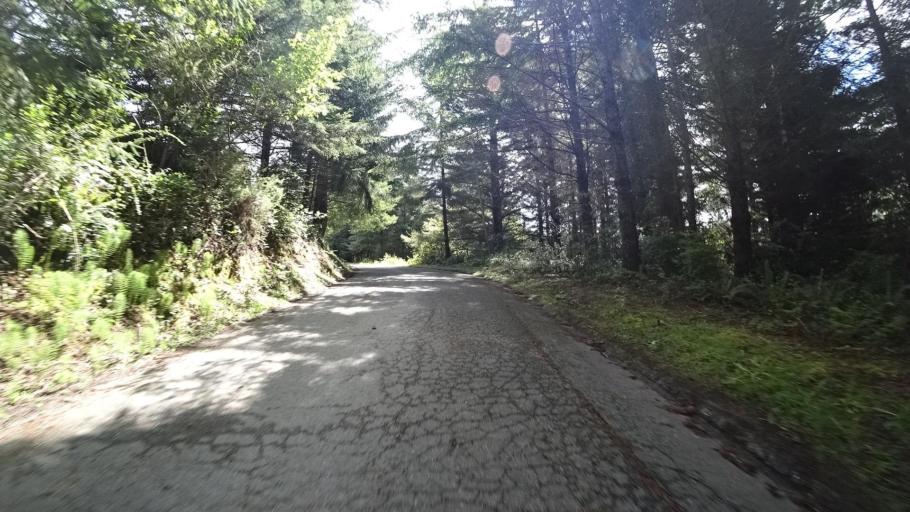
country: US
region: California
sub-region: Humboldt County
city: Arcata
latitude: 40.9105
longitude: -124.0455
